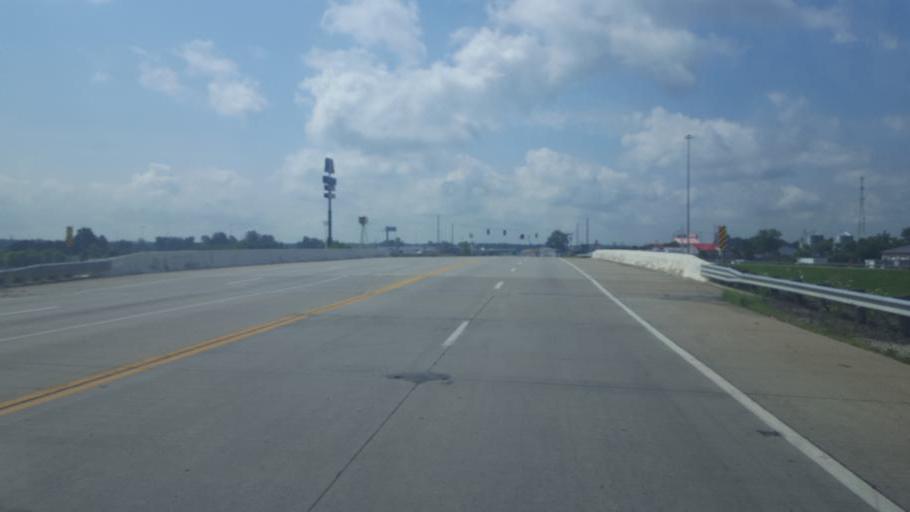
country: US
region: Ohio
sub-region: Fairfield County
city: Millersport
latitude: 39.9429
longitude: -82.5355
